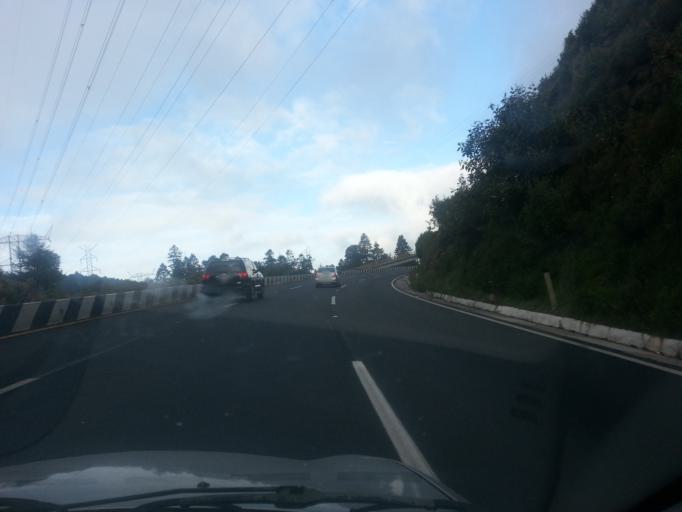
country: MX
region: Mexico City
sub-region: Cuajimalpa de Morelos
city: San Lorenzo Acopilco
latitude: 19.2964
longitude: -99.3503
